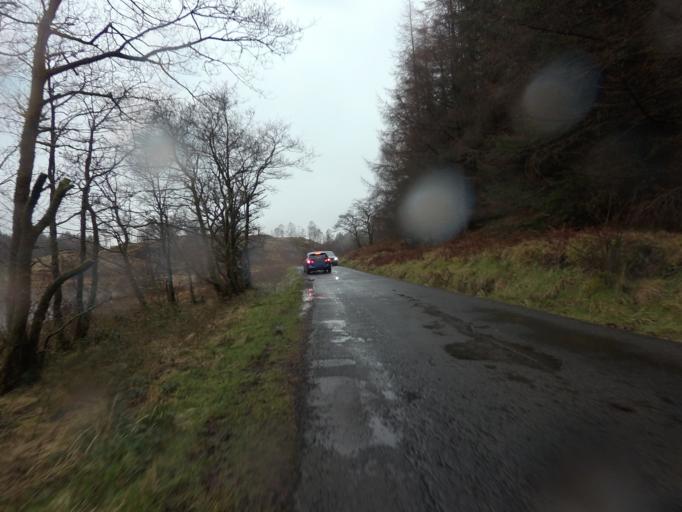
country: GB
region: Scotland
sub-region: West Dunbartonshire
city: Balloch
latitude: 56.2017
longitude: -4.5290
